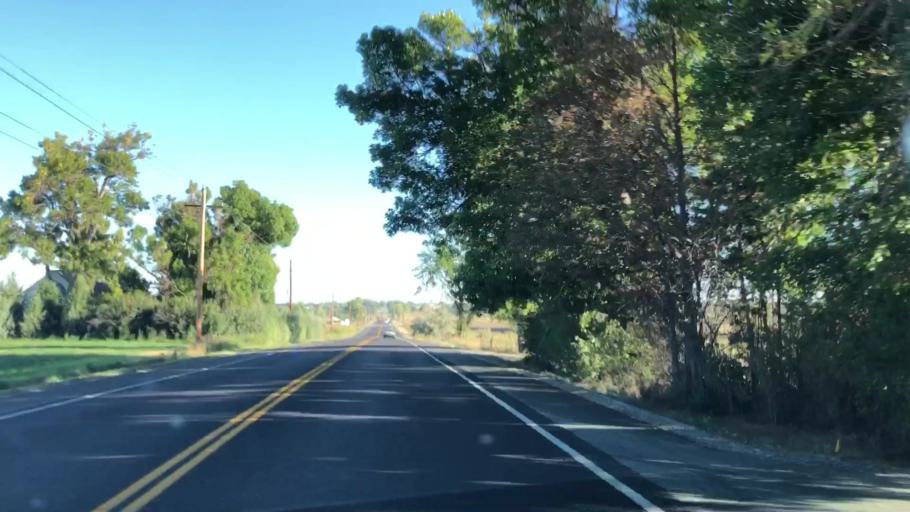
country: US
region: Colorado
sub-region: Larimer County
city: Loveland
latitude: 40.4740
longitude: -105.0394
